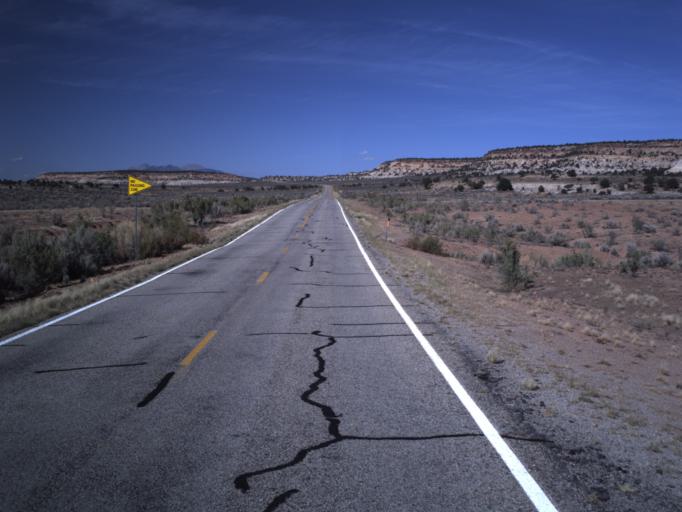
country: US
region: Utah
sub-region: San Juan County
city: Monticello
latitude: 38.0278
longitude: -109.4231
